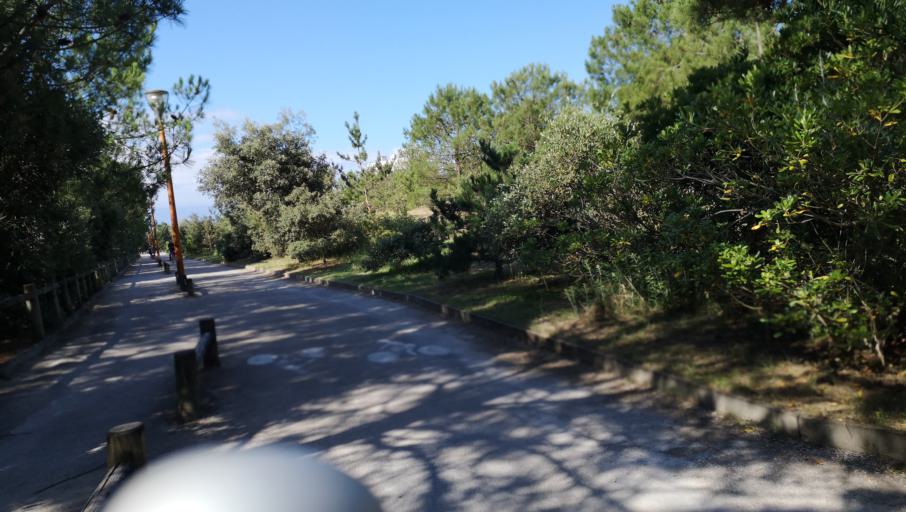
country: FR
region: Pays de la Loire
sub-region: Departement de la Vendee
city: Les Sables-d'Olonne
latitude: 46.4868
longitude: -1.7624
